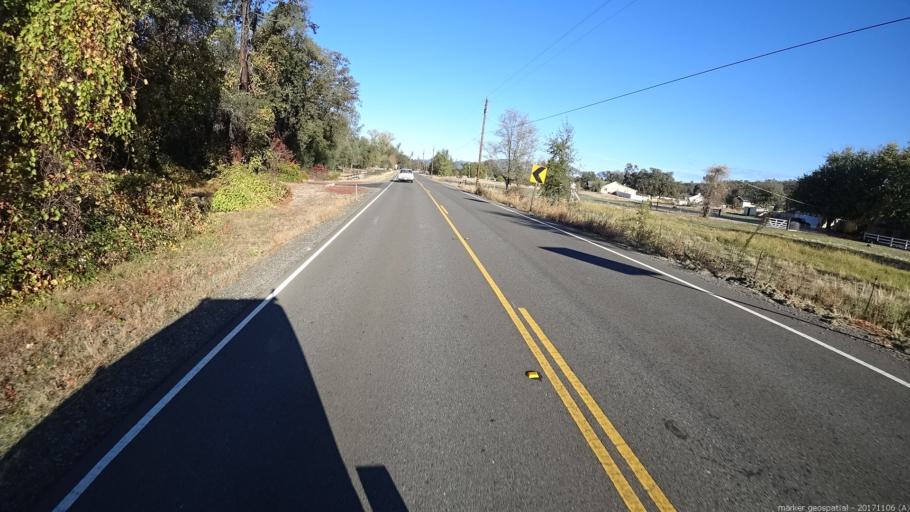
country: US
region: California
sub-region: Shasta County
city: Bella Vista
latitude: 40.6251
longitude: -122.2332
